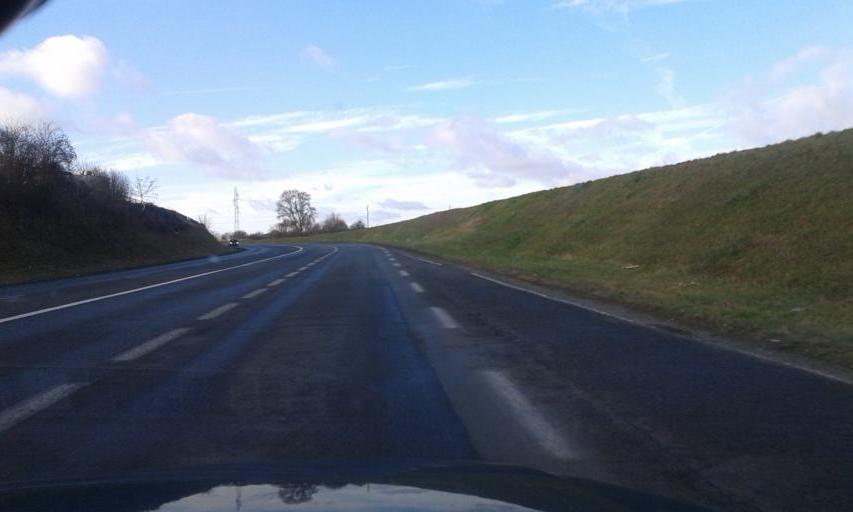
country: FR
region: Picardie
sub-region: Departement de l'Oise
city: Venette
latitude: 49.4100
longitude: 2.7846
